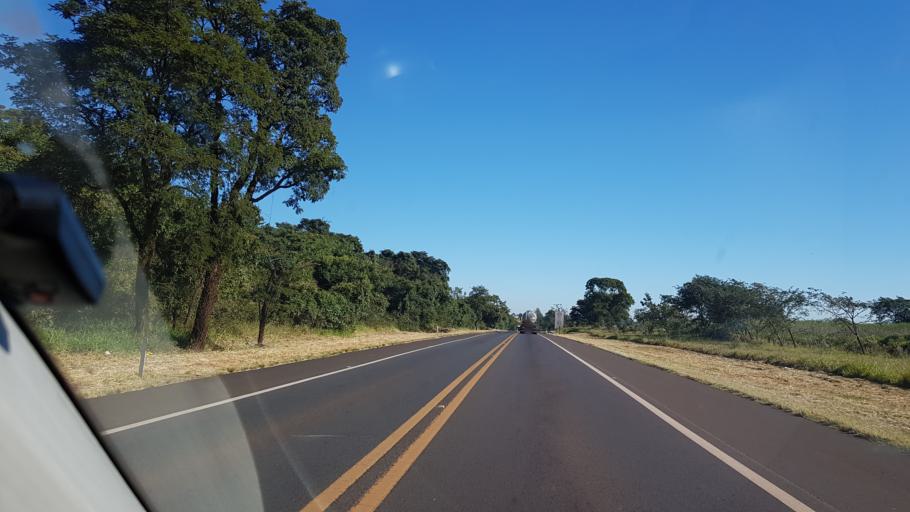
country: BR
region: Sao Paulo
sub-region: Assis
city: Assis
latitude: -22.5847
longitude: -50.5010
